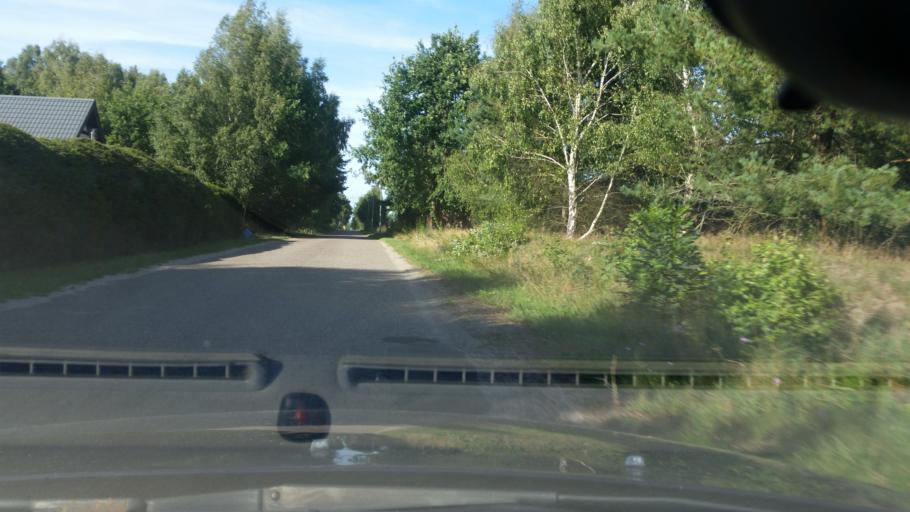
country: PL
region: Pomeranian Voivodeship
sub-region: Powiat wejherowski
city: Choczewo
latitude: 54.7635
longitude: 17.7928
